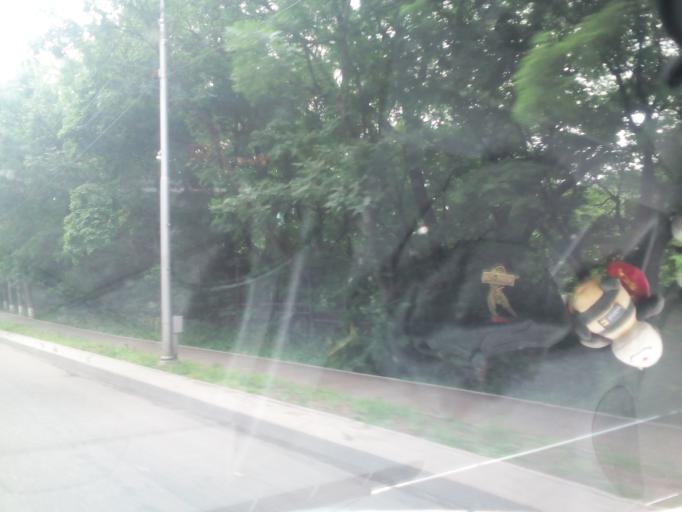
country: RU
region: Stavropol'skiy
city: Zheleznovodsk
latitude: 44.1373
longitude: 43.0158
